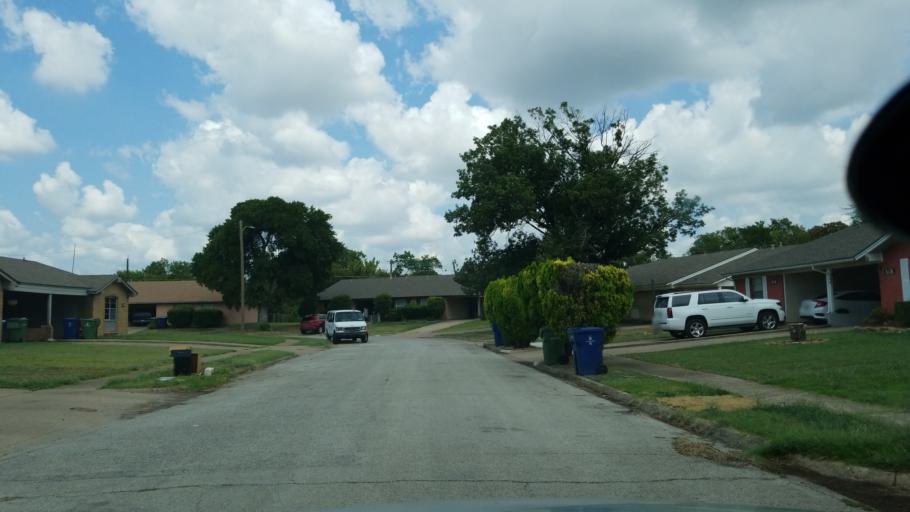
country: US
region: Texas
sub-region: Dallas County
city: Garland
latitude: 32.9149
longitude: -96.6536
